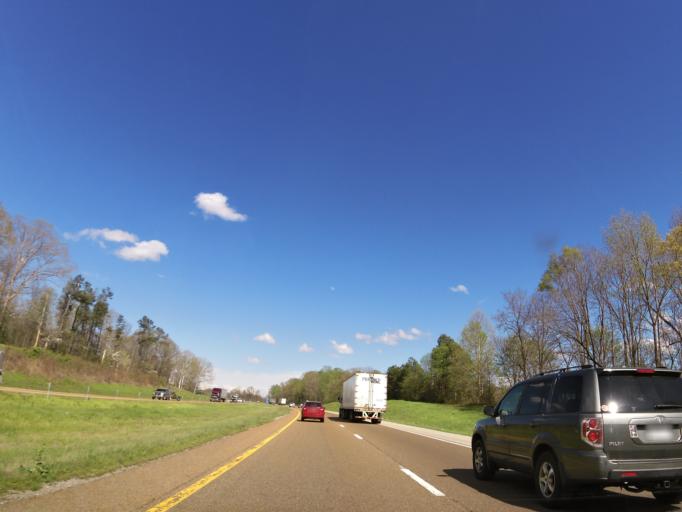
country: US
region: Tennessee
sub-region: Madison County
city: Jackson
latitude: 35.6809
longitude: -88.7364
